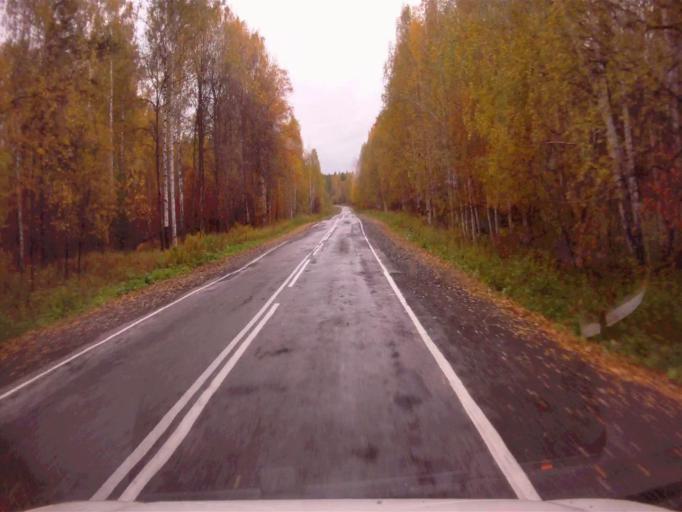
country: RU
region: Chelyabinsk
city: Nizhniy Ufaley
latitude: 56.0548
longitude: 59.9572
